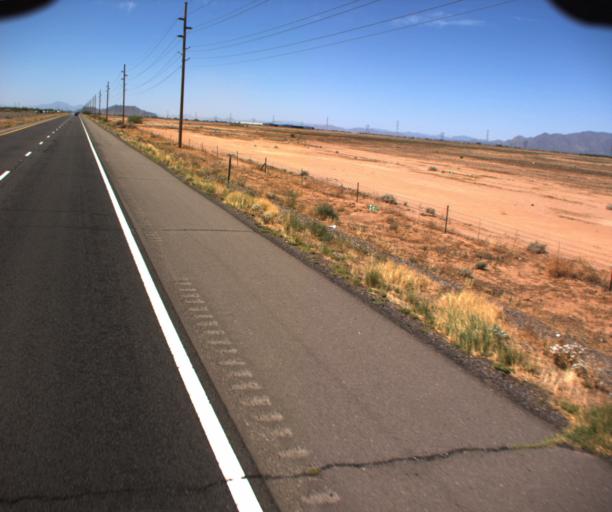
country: US
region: Arizona
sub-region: Maricopa County
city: Sun Lakes
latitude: 33.2332
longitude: -111.9844
